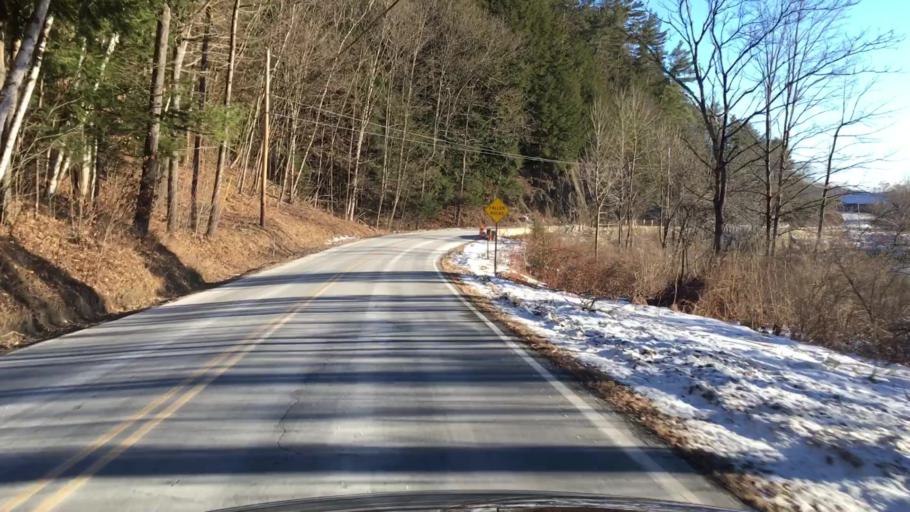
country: US
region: New Hampshire
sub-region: Grafton County
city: Woodsville
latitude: 44.1635
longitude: -72.0418
